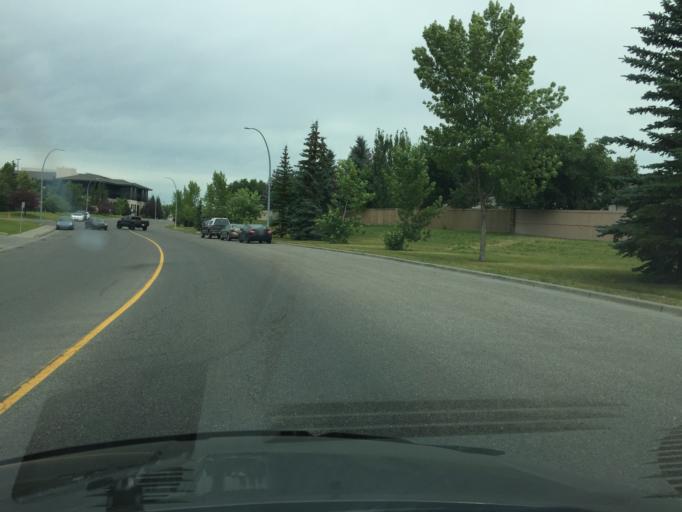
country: CA
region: Alberta
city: Calgary
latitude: 50.9323
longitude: -114.0650
